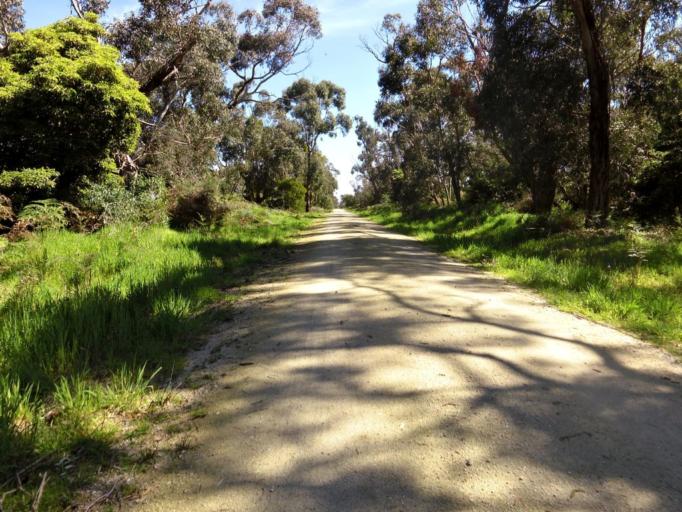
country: AU
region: Victoria
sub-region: Latrobe
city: Morwell
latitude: -38.6724
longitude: 146.4057
